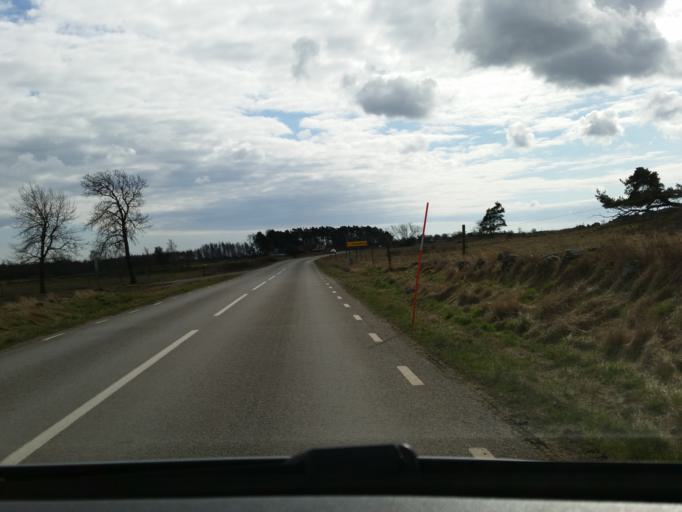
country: SE
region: Kalmar
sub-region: Morbylanga Kommun
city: Sodra Sandby
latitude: 56.6615
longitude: 16.6814
